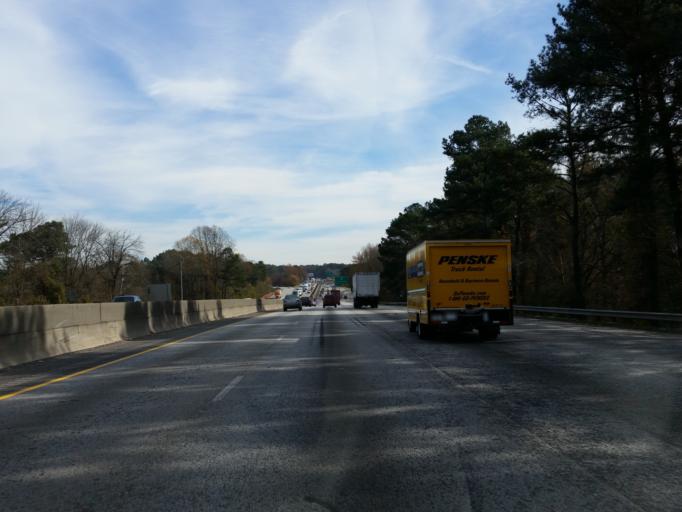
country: US
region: Georgia
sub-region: Cobb County
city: Mableton
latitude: 33.7689
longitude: -84.5364
